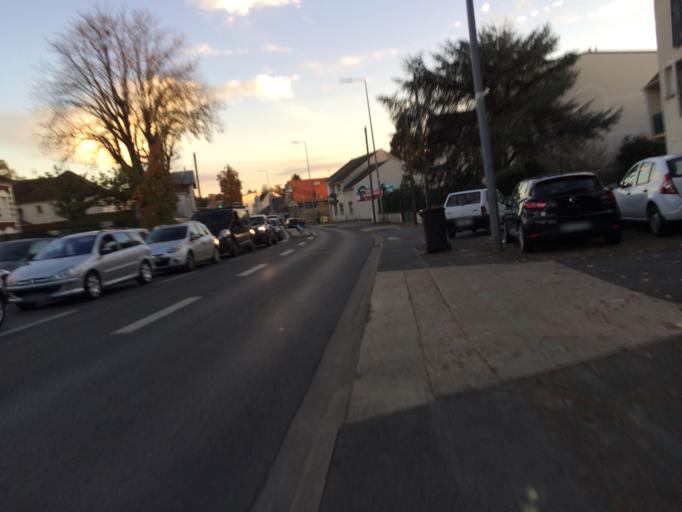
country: FR
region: Ile-de-France
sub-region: Departement de l'Essonne
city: Sainte-Genevieve-des-Bois
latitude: 48.6356
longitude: 2.3333
